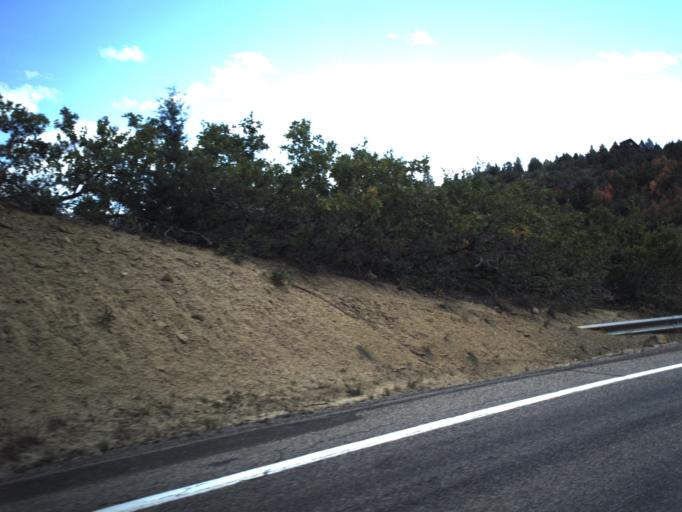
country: US
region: Utah
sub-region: Garfield County
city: Panguitch
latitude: 37.4902
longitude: -112.5275
